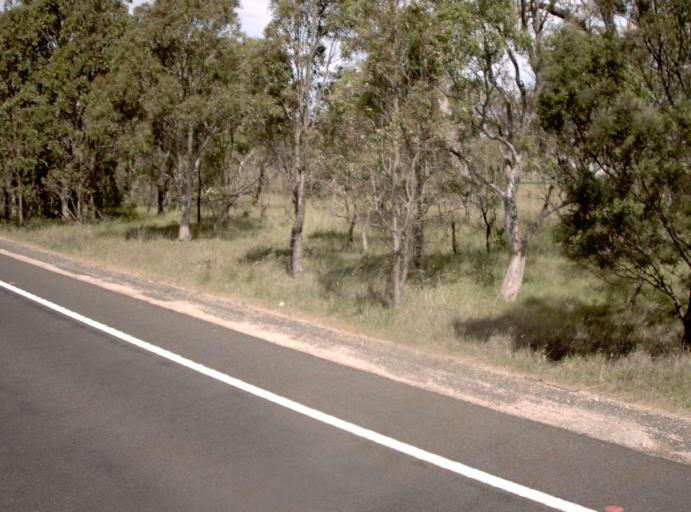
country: AU
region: Victoria
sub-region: East Gippsland
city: Bairnsdale
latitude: -37.8670
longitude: 147.4864
